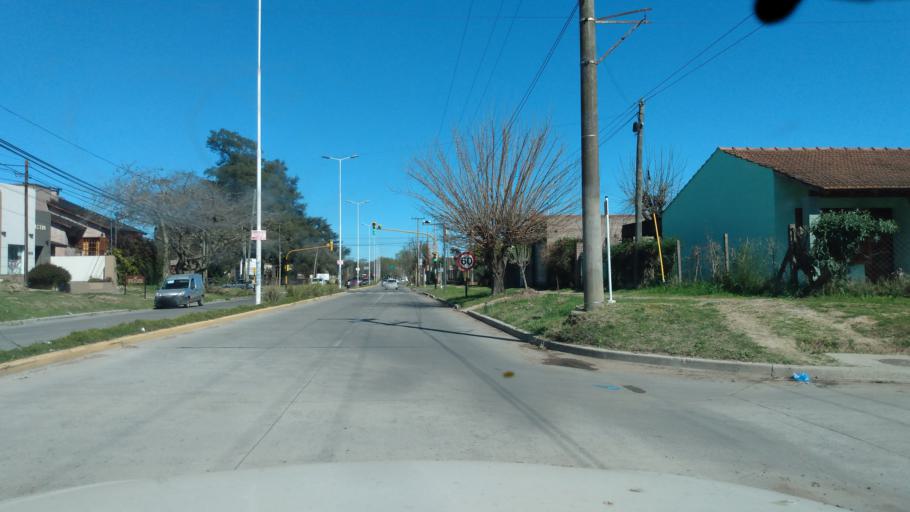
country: AR
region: Buenos Aires
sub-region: Partido de Lujan
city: Lujan
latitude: -34.5587
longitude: -59.1057
